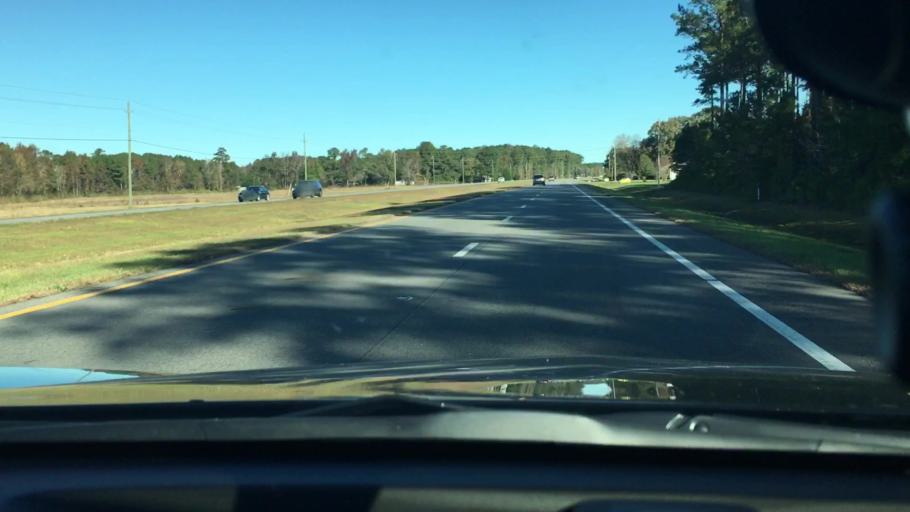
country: US
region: North Carolina
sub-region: Pitt County
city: Greenville
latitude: 35.6842
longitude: -77.3655
